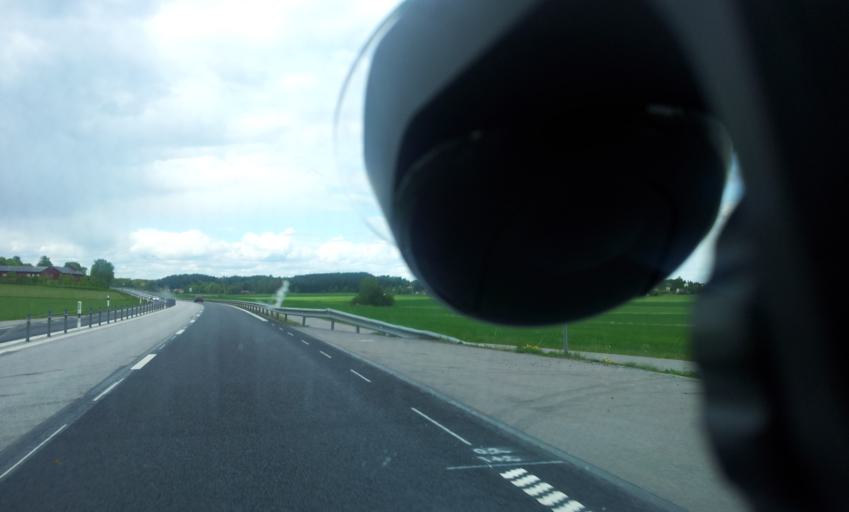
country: SE
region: OEstergoetland
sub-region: Soderkopings Kommun
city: Soederkoeping
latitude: 58.5357
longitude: 16.2824
